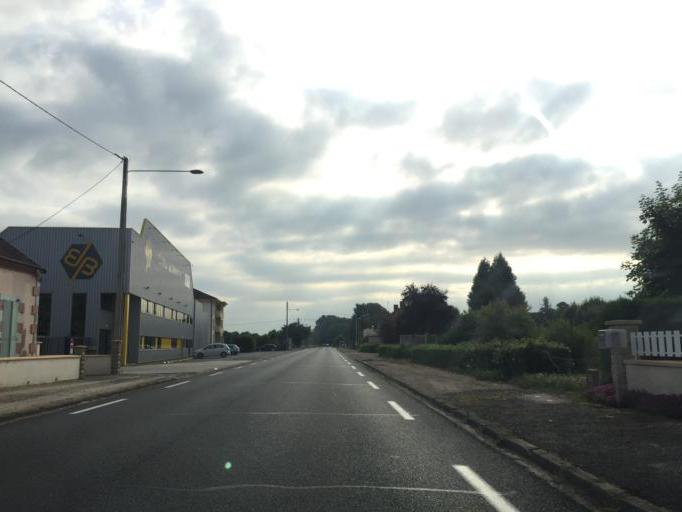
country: FR
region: Auvergne
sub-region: Departement de l'Allier
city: Molinet
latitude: 46.4734
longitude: 3.9553
